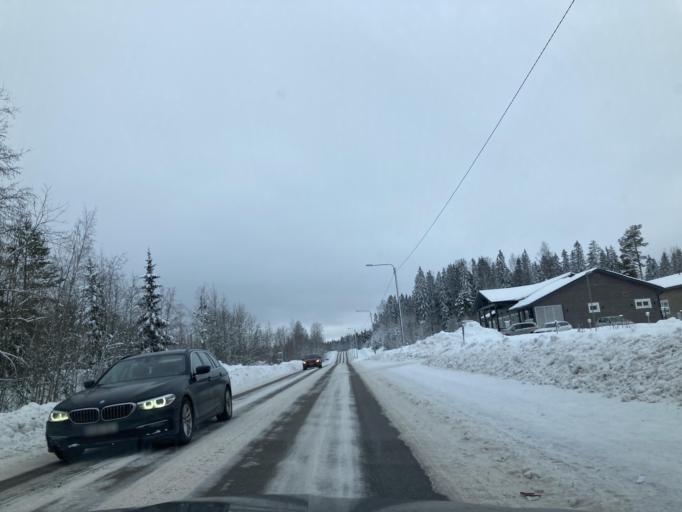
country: FI
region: Central Finland
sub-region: Jaemsae
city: Jaemsae
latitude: 61.8807
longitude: 25.2851
